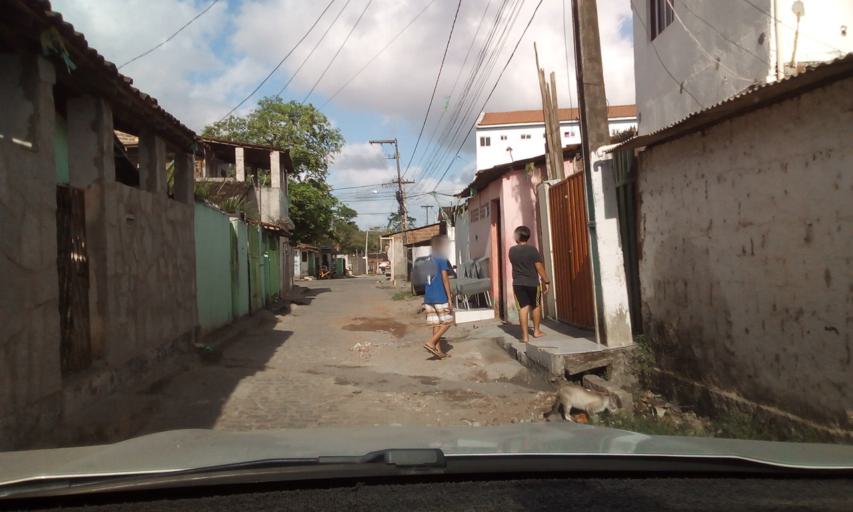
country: BR
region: Paraiba
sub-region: Bayeux
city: Bayeux
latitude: -7.1515
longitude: -34.9052
